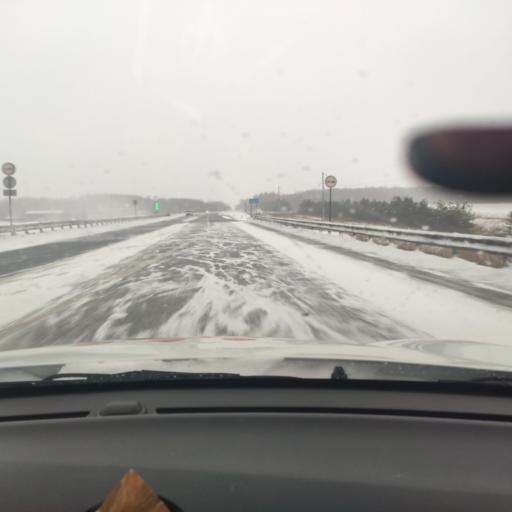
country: RU
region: Tatarstan
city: Verkhniy Uslon
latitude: 55.7131
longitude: 48.8750
